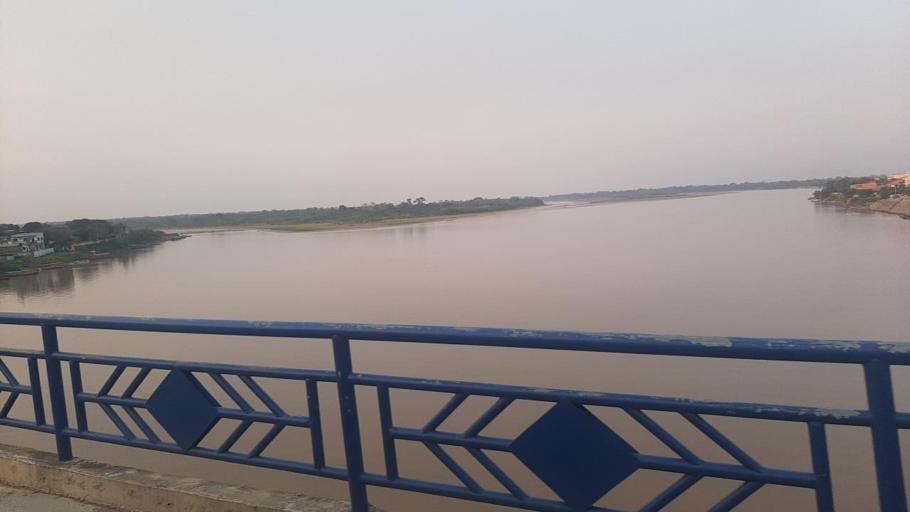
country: BO
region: El Beni
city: Rurrenabaque
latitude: -14.4434
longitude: -67.5339
